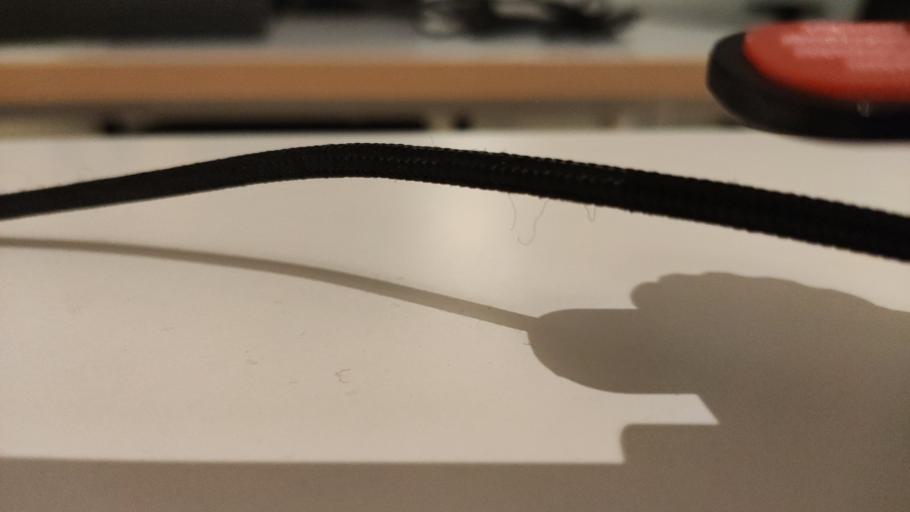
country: RU
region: Moskovskaya
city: Shaburnovo
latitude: 56.4256
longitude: 37.9600
